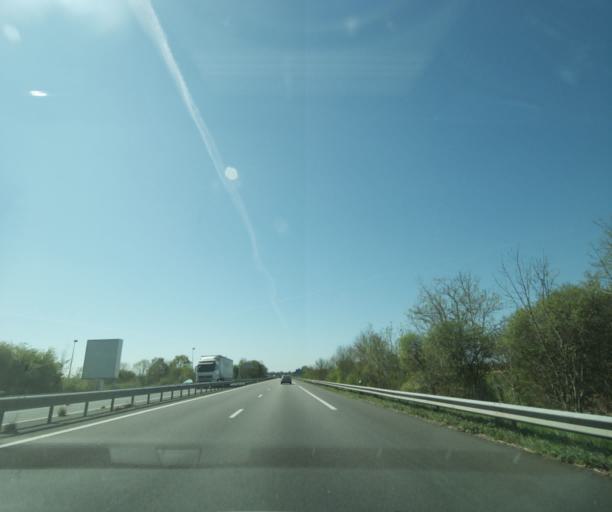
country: FR
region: Centre
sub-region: Departement de l'Indre
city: Luant
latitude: 46.7225
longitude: 1.6019
